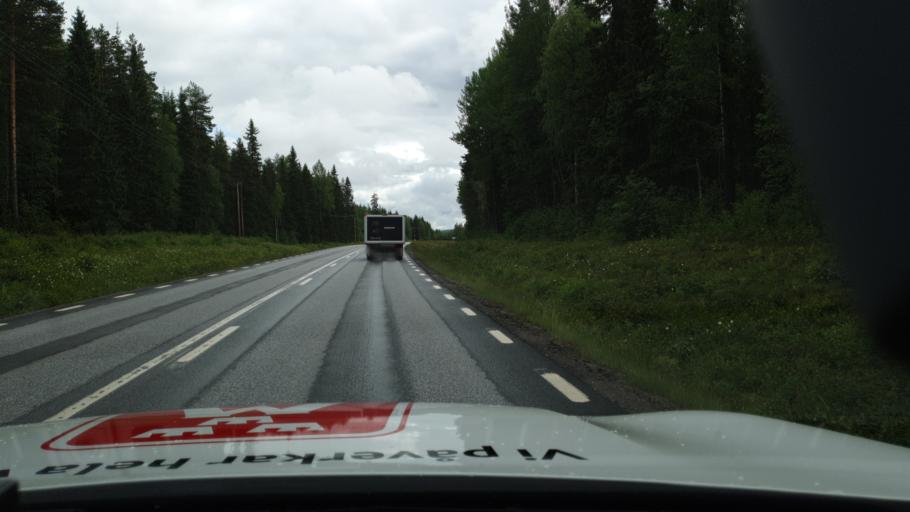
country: SE
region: Vaesterbotten
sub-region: Vannas Kommun
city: Vaennaes
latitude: 63.9396
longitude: 19.7716
